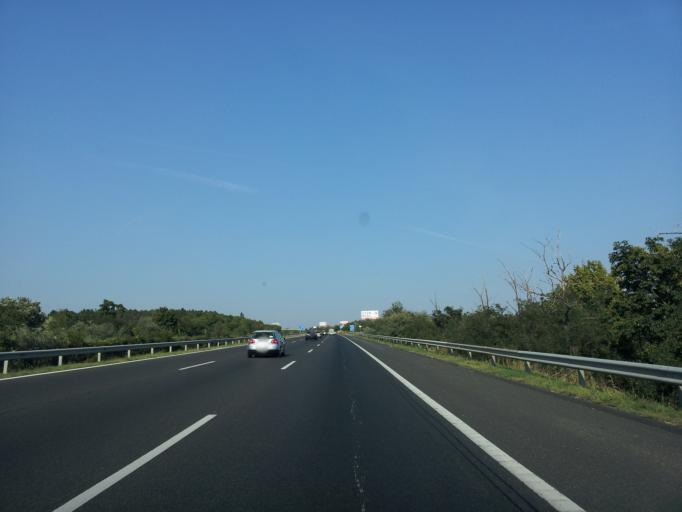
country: HU
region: Pest
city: Tarnok
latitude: 47.3941
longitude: 18.8586
